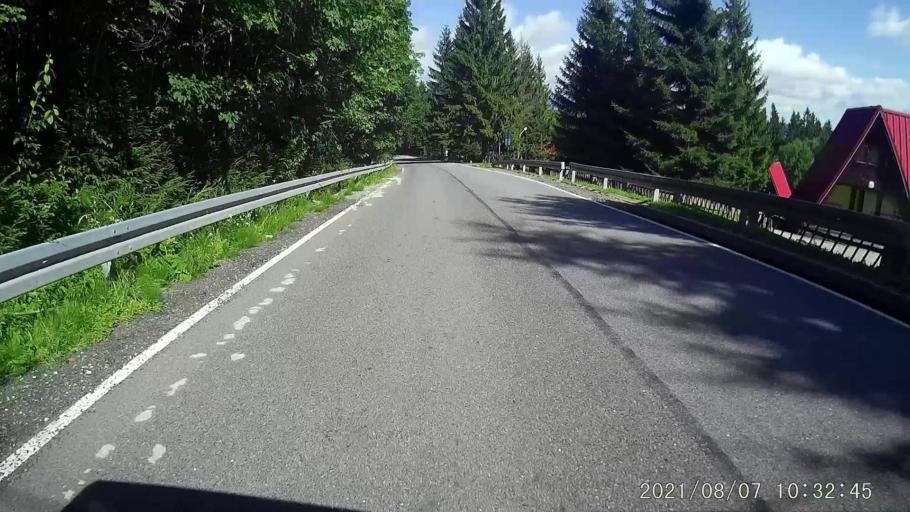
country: PL
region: Lower Silesian Voivodeship
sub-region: Powiat klodzki
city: Duszniki-Zdroj
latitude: 50.3870
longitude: 16.3604
